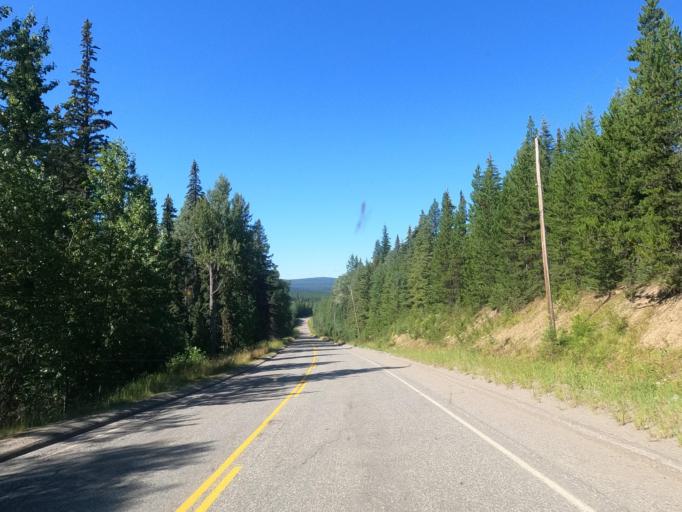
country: CA
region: British Columbia
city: Quesnel
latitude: 53.0220
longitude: -122.0645
